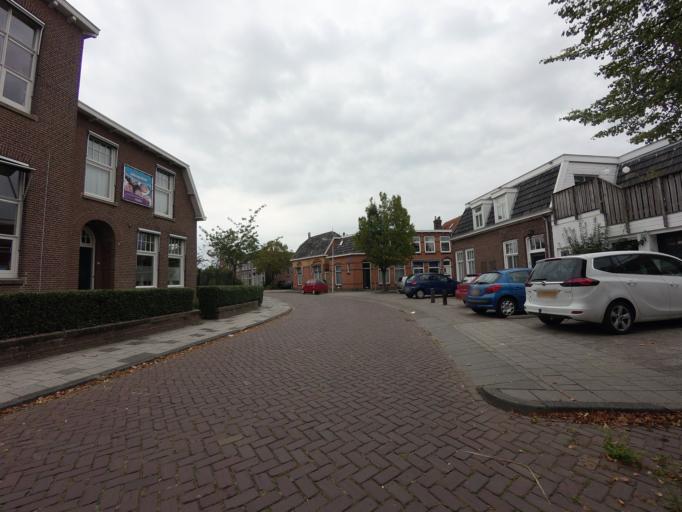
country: NL
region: Friesland
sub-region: Sudwest Fryslan
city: Sneek
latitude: 53.0346
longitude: 5.6605
